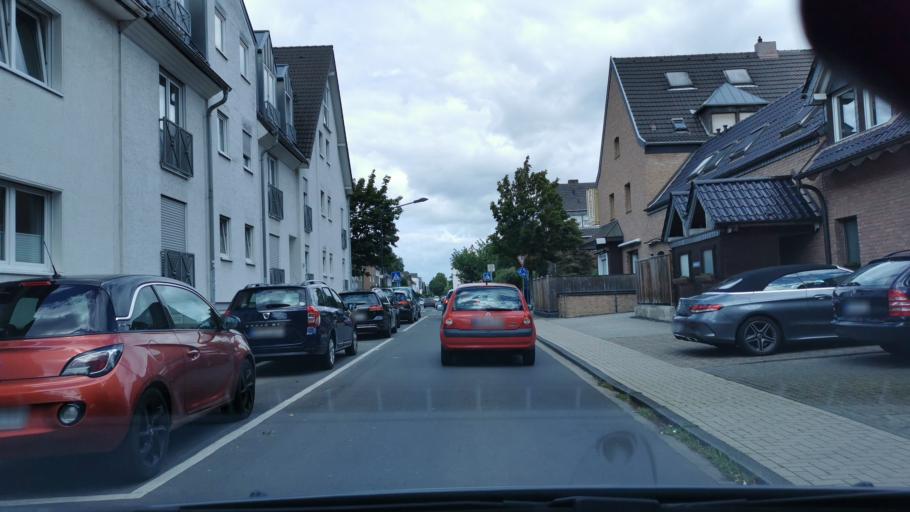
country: DE
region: North Rhine-Westphalia
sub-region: Regierungsbezirk Koln
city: Hurth
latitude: 50.8977
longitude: 6.8956
